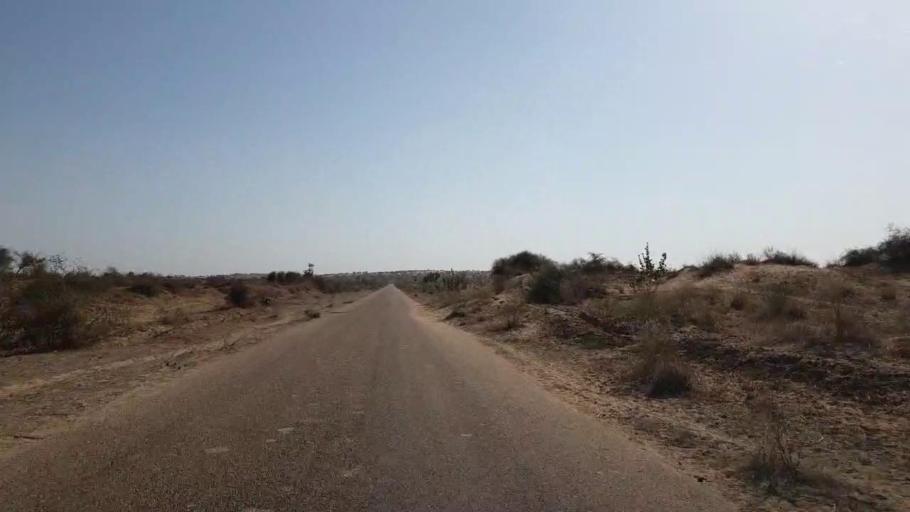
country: PK
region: Sindh
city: Islamkot
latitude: 25.0725
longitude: 70.0428
